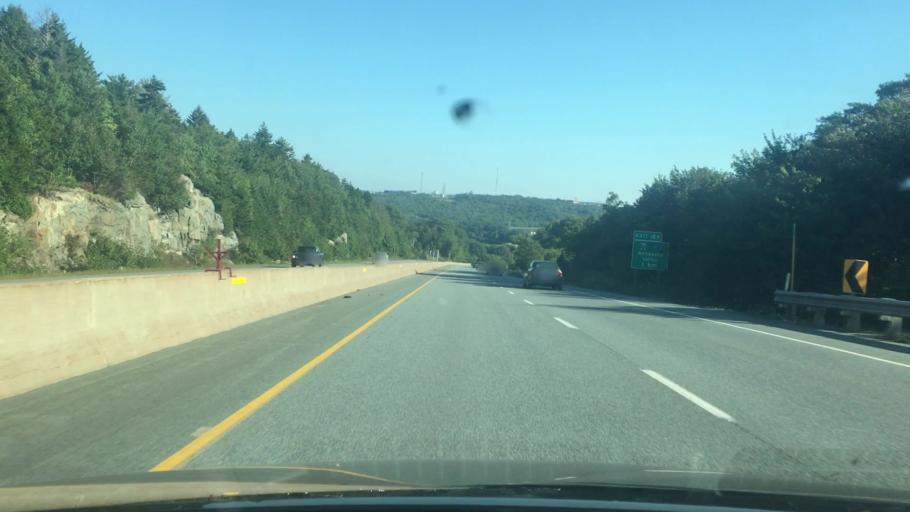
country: CA
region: Nova Scotia
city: Dartmouth
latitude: 44.7367
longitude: -63.6619
